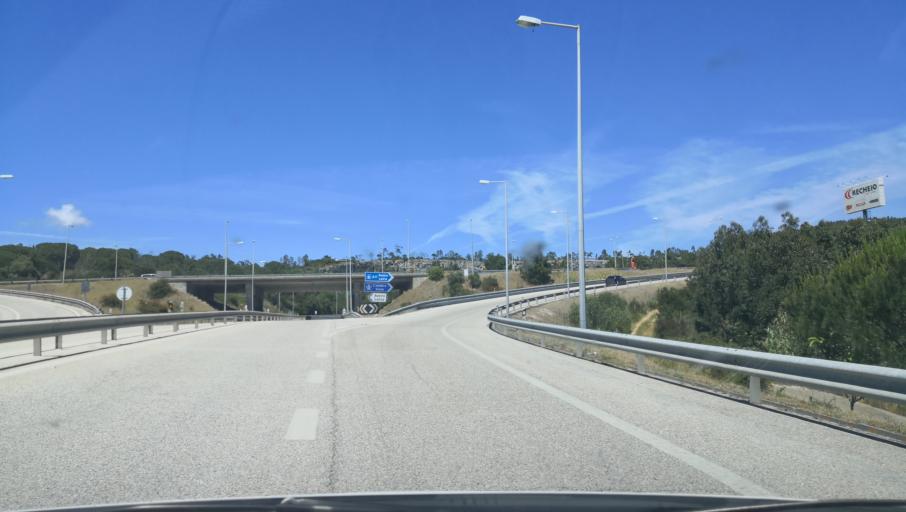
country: PT
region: Coimbra
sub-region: Figueira da Foz
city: Tavarede
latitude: 40.1486
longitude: -8.8323
